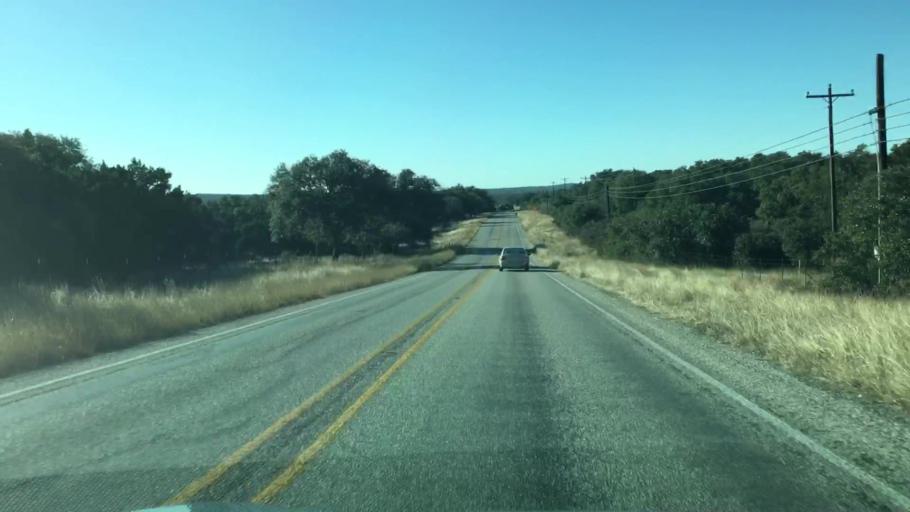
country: US
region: Texas
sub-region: Blanco County
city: Blanco
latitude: 30.1033
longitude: -98.3470
